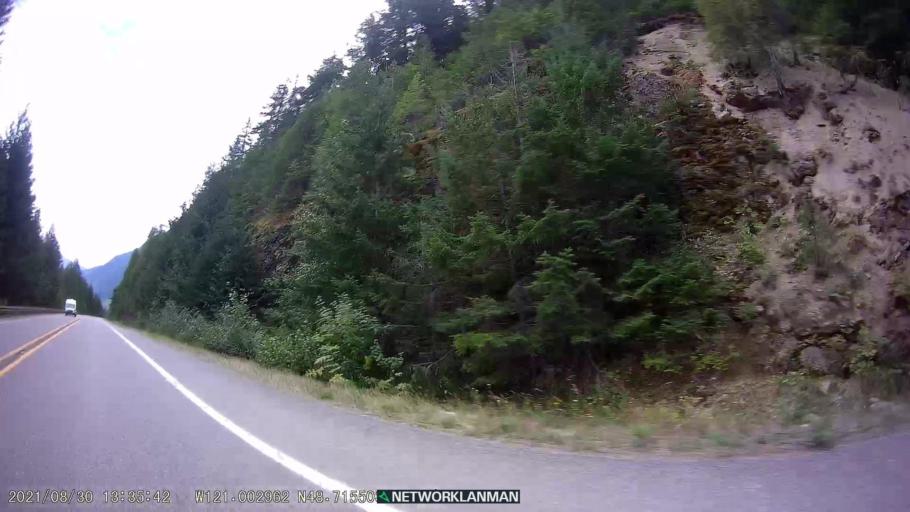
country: US
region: Washington
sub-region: Snohomish County
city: Darrington
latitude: 48.7150
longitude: -121.0029
